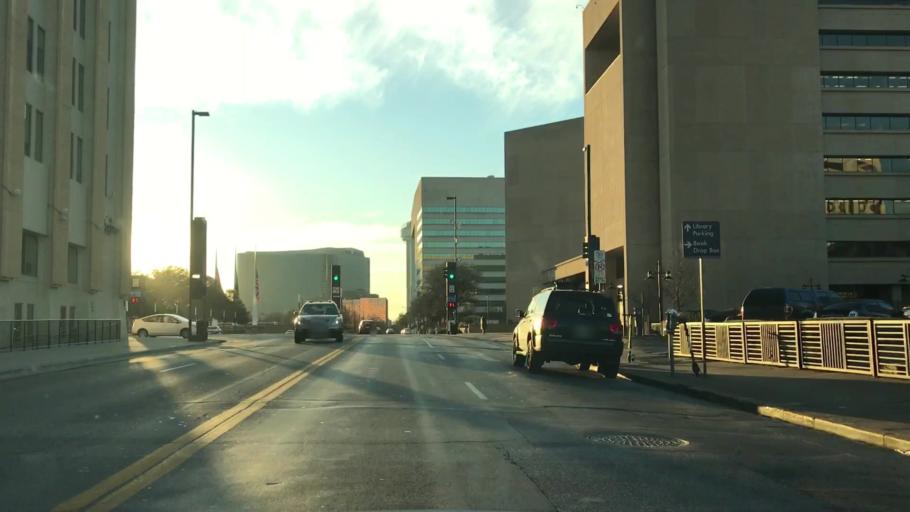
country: US
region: Texas
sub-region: Dallas County
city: Dallas
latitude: 32.7781
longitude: -96.7956
